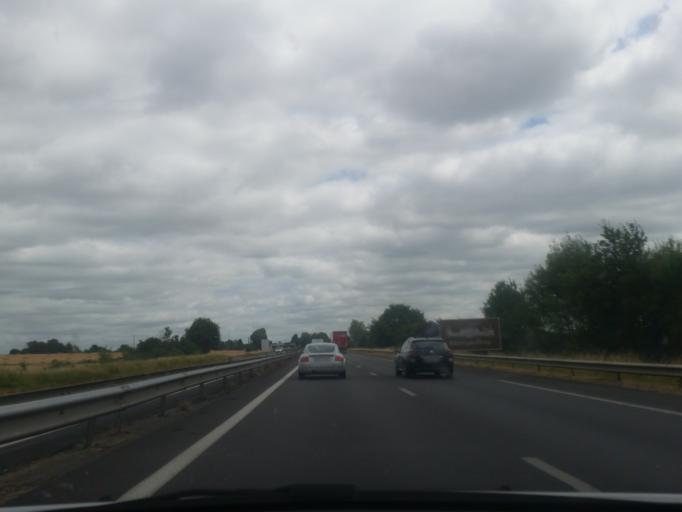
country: FR
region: Pays de la Loire
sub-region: Departement de Maine-et-Loire
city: Pellouailles-les-Vignes
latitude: 47.5026
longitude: -0.4663
